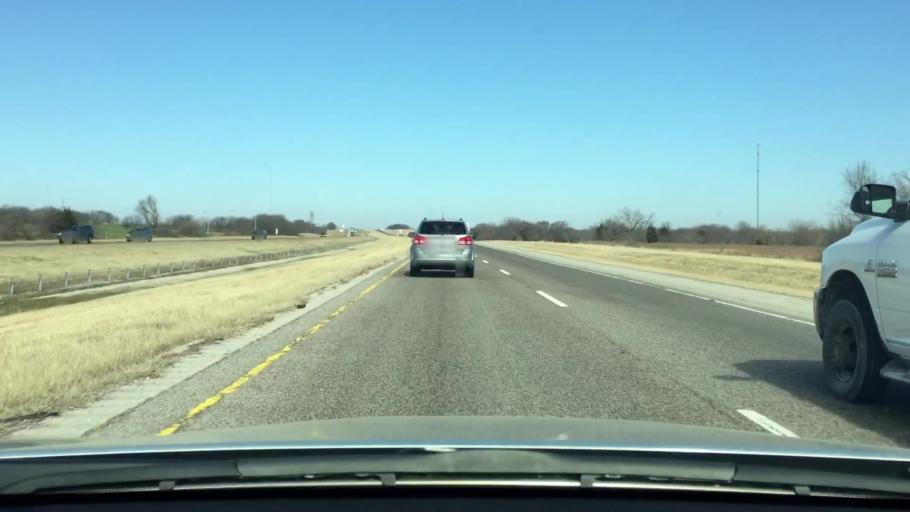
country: US
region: Oklahoma
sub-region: McClain County
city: Purcell
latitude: 34.9205
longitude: -97.3572
